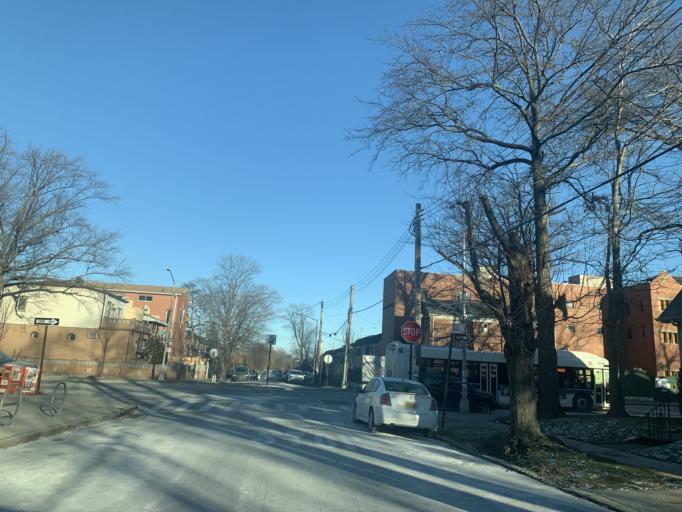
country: US
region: New York
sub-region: Queens County
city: Jamaica
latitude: 40.7213
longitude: -73.8194
